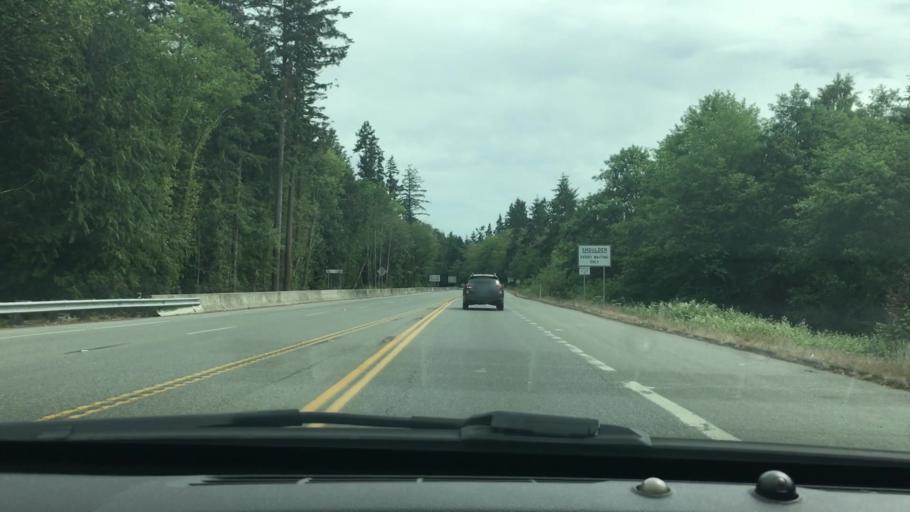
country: US
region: Washington
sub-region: Kitsap County
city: Bainbridge Island
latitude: 47.6348
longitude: -122.5158
